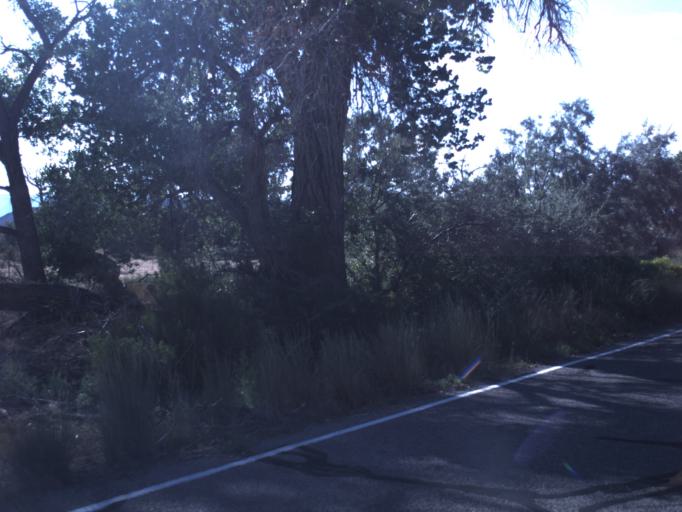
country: US
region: Utah
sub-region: Emery County
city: Huntington
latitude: 39.4190
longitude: -110.8577
